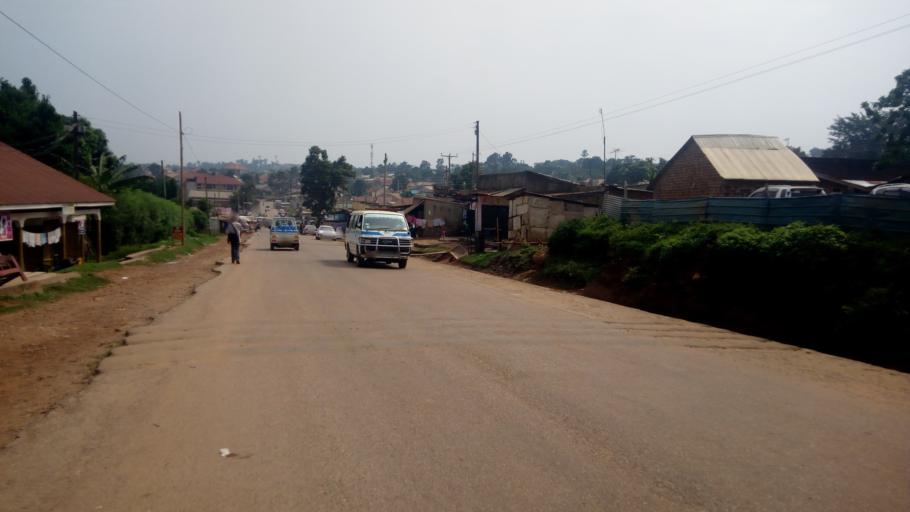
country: UG
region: Central Region
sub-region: Wakiso District
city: Kireka
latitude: 0.3070
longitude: 32.6550
